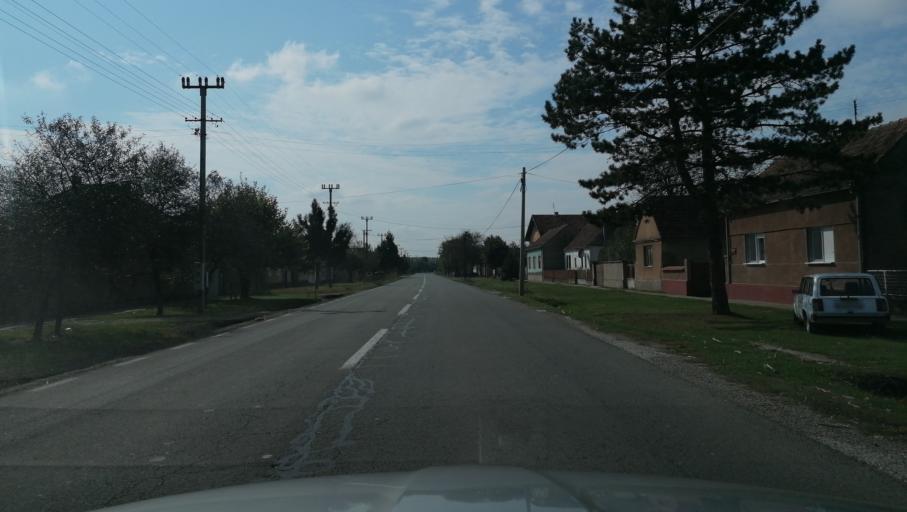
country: RS
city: Bosut
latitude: 44.9328
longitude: 19.3644
